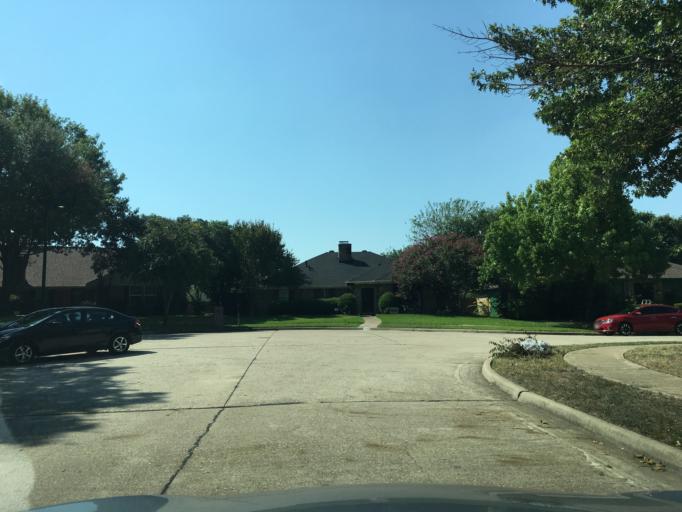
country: US
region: Texas
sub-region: Dallas County
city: Garland
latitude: 32.9354
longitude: -96.6357
